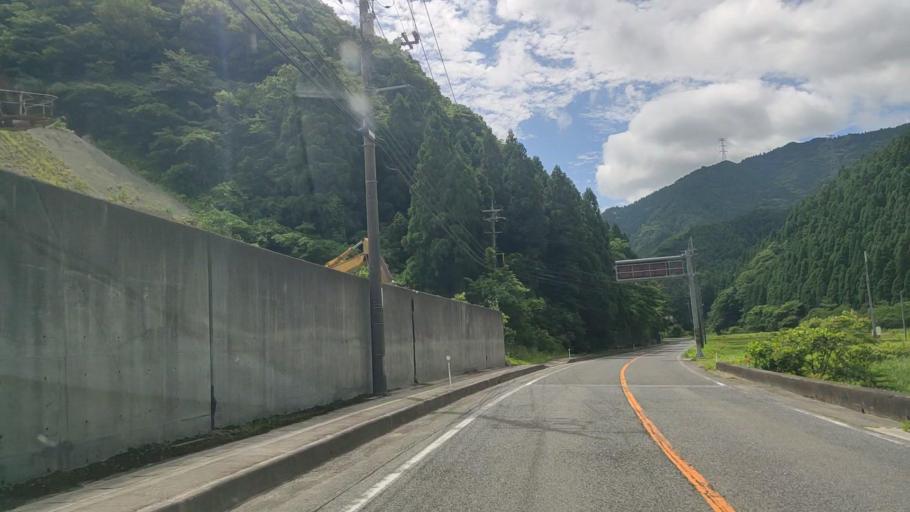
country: JP
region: Okayama
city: Niimi
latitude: 35.2210
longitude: 133.4515
